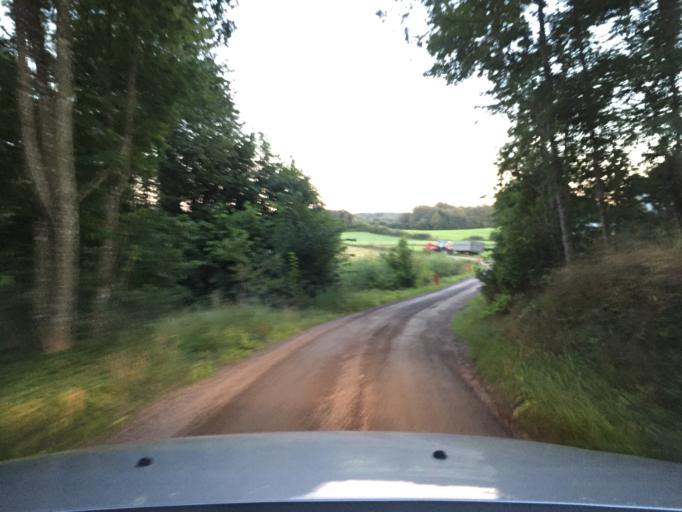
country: SE
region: Skane
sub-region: Hassleholms Kommun
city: Sosdala
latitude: 55.9950
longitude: 13.6693
